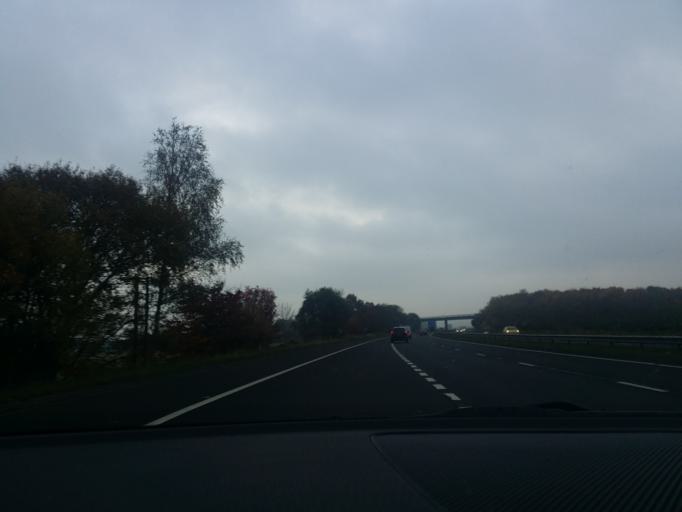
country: GB
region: Scotland
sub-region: Falkirk
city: Airth
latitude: 56.0483
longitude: -3.7769
